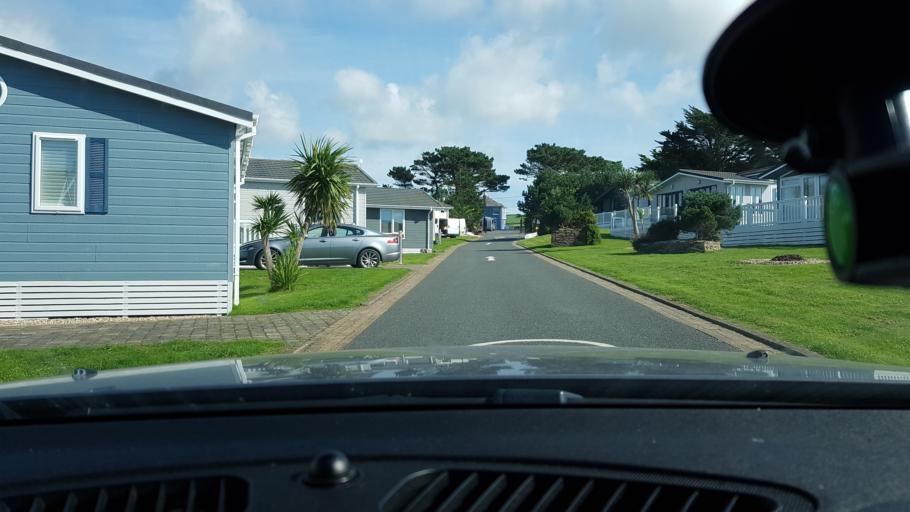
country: GB
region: England
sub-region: Cornwall
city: Tintagel
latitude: 50.6682
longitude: -4.7388
